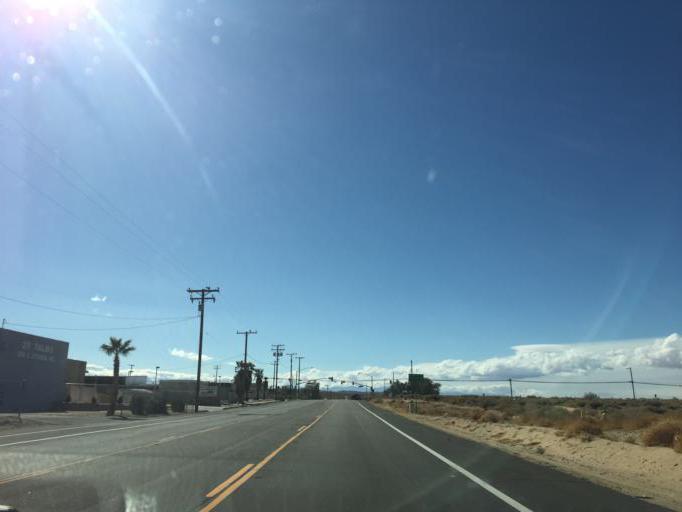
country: US
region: California
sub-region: San Bernardino County
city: Twentynine Palms
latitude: 34.1648
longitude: -116.0515
